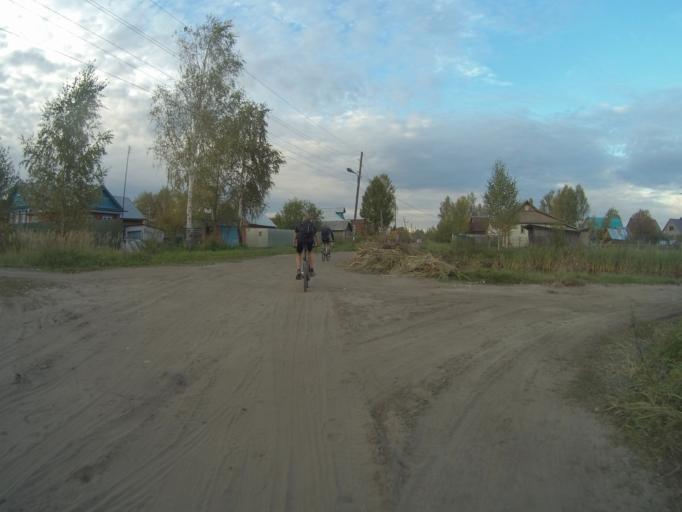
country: RU
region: Vladimir
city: Sobinka
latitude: 55.9795
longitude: 40.0097
